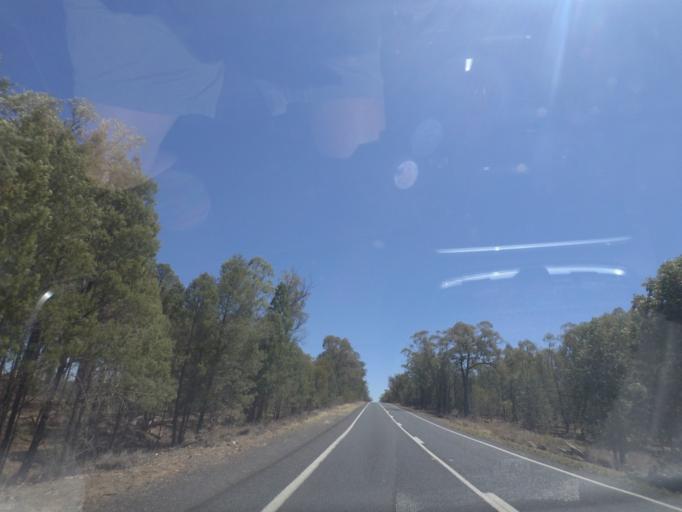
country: AU
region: New South Wales
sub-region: Gilgandra
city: Gilgandra
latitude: -31.4843
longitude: 148.8821
